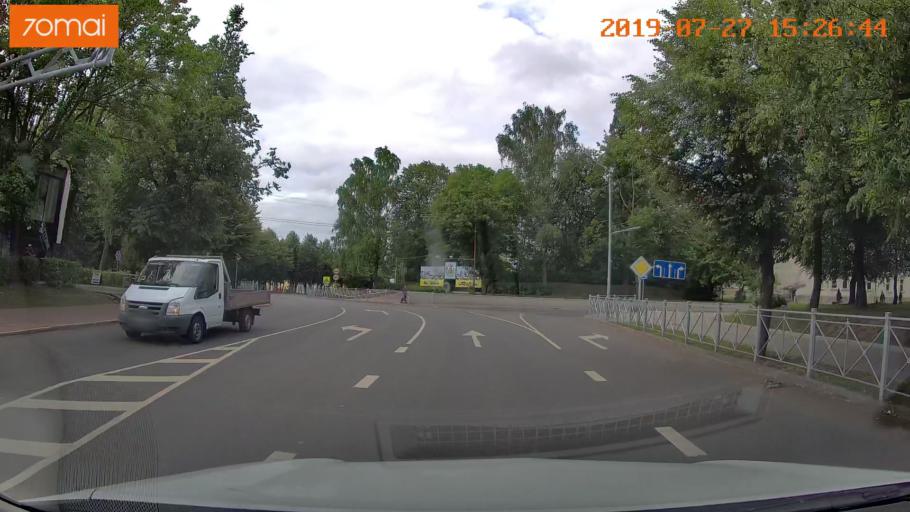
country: RU
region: Kaliningrad
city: Nesterov
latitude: 54.6326
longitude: 22.5700
